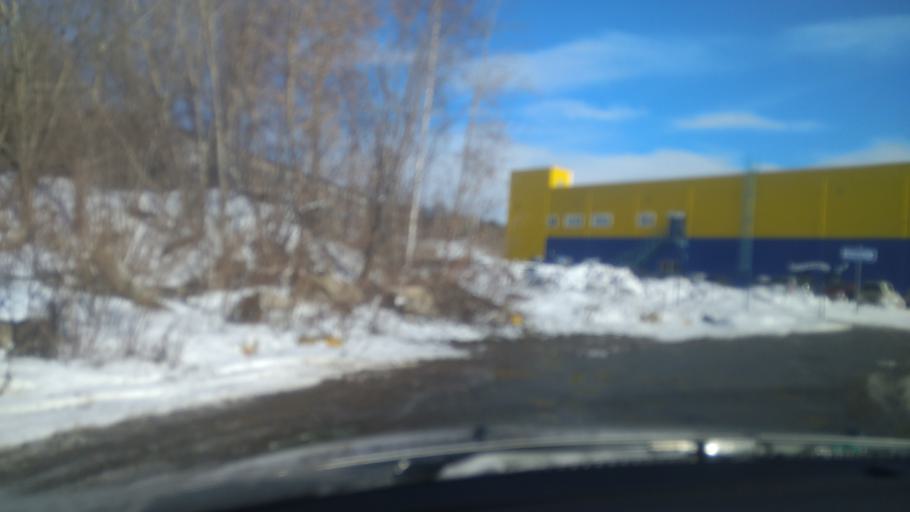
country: RU
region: Sverdlovsk
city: Istok
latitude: 56.8251
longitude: 60.7071
